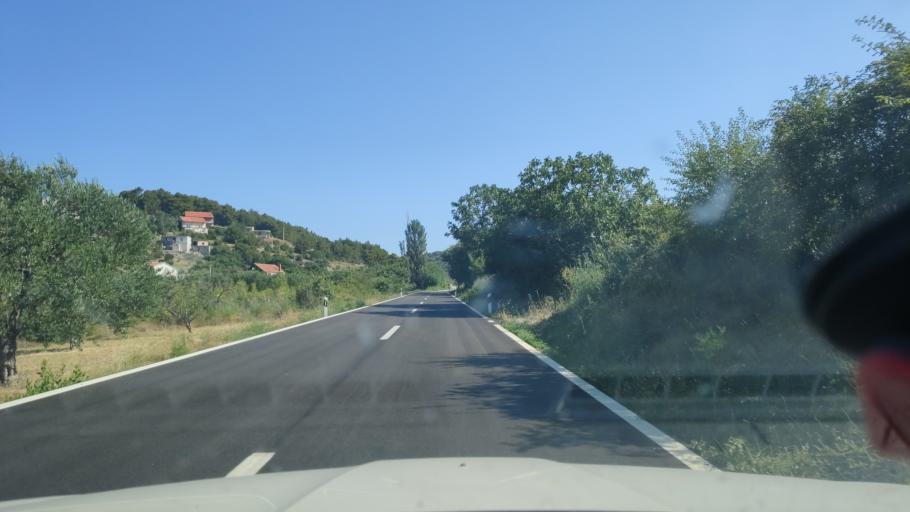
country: HR
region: Sibensko-Kniniska
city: Zaton
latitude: 43.8493
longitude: 15.8970
